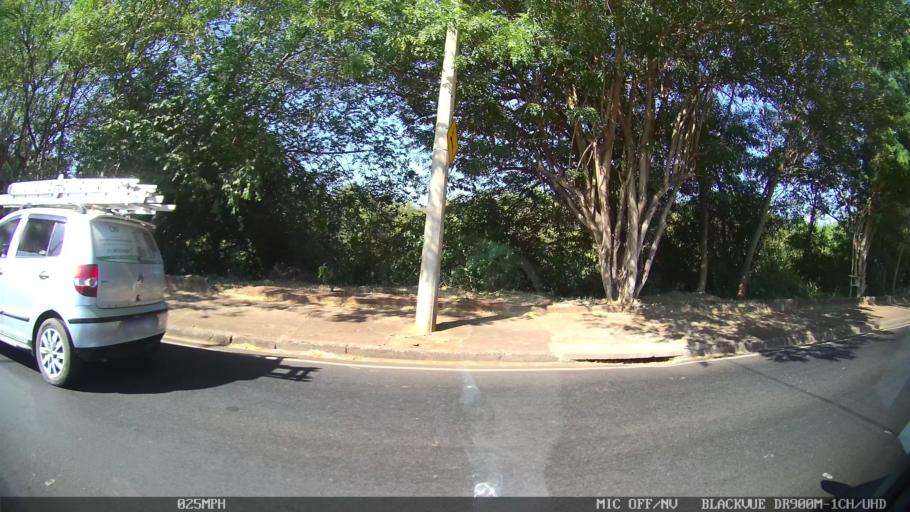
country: BR
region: Sao Paulo
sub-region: Sao Jose Do Rio Preto
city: Sao Jose do Rio Preto
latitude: -20.8046
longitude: -49.4213
